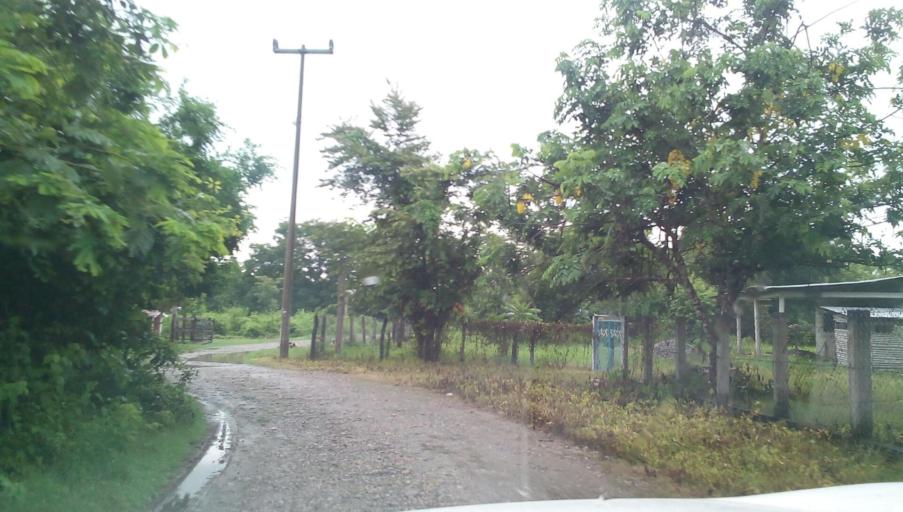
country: MX
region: Veracruz
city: Tempoal de Sanchez
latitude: 21.4190
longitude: -98.4317
